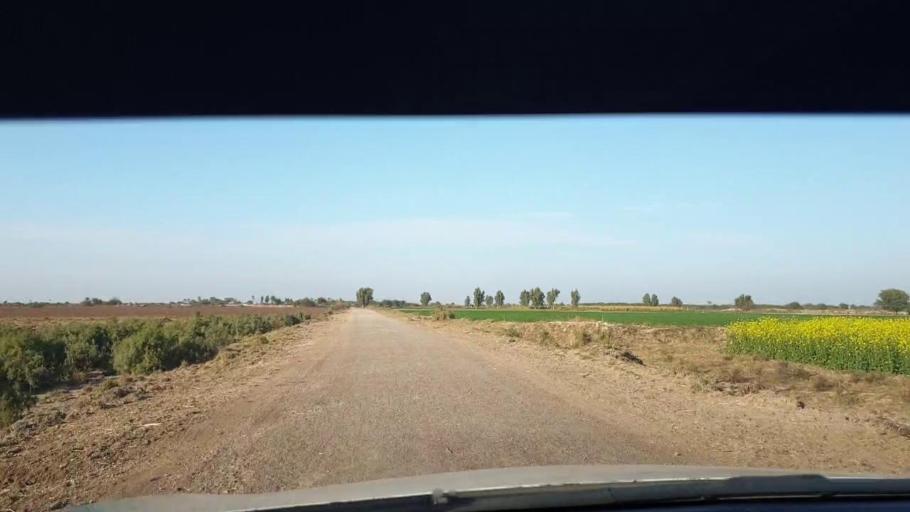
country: PK
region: Sindh
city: Berani
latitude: 25.8165
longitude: 68.9099
